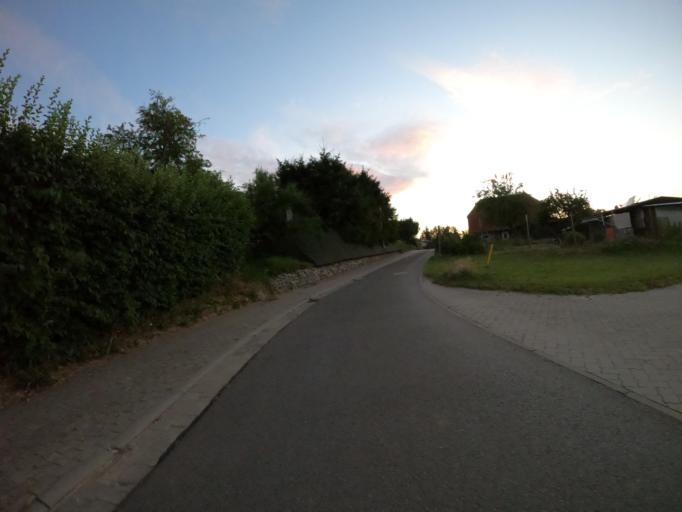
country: DE
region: Mecklenburg-Vorpommern
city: Woldegk
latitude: 53.4559
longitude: 13.5843
